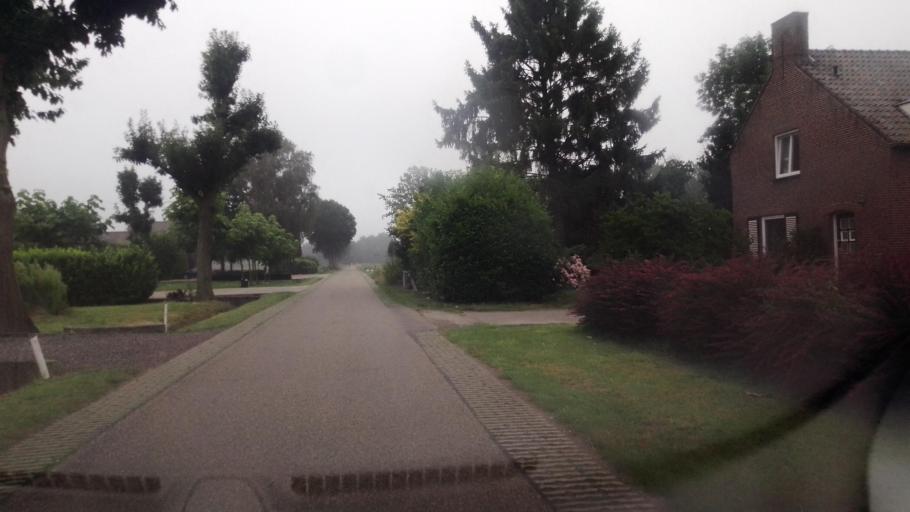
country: NL
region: Limburg
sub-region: Gemeente Peel en Maas
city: Maasbree
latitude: 51.4296
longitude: 6.0286
